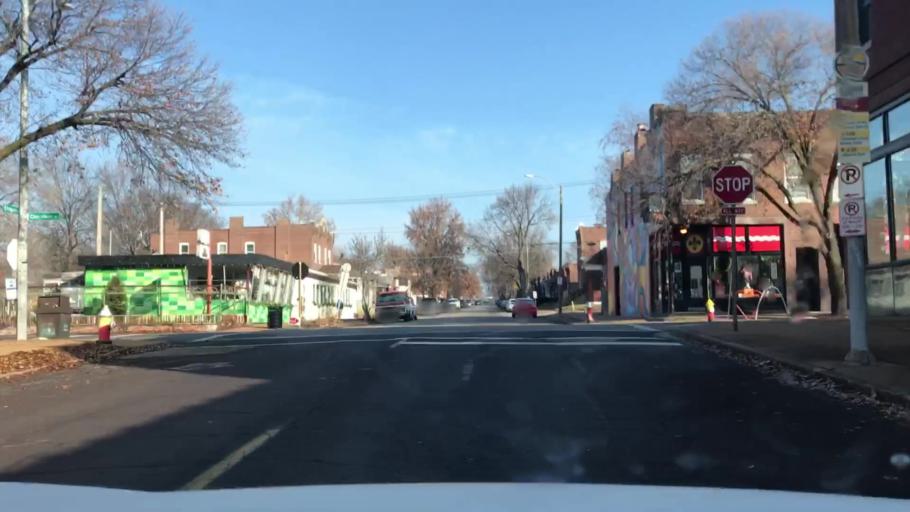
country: US
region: Missouri
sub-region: City of Saint Louis
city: St. Louis
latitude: 38.5945
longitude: -90.2369
